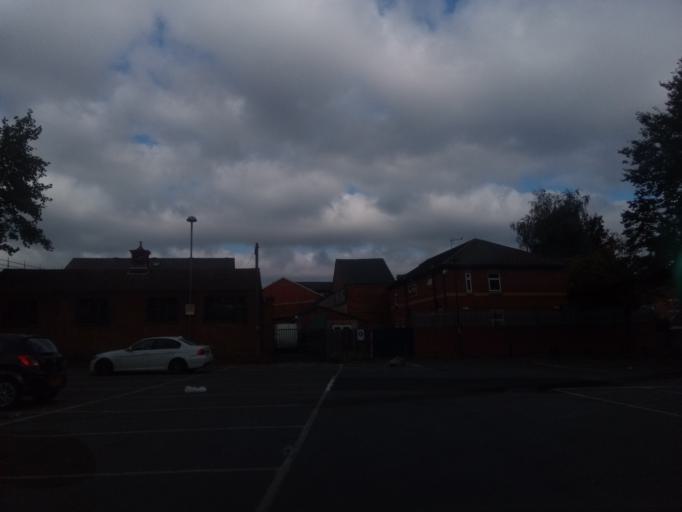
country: GB
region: England
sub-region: Derby
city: Derby
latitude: 52.9133
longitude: -1.4764
